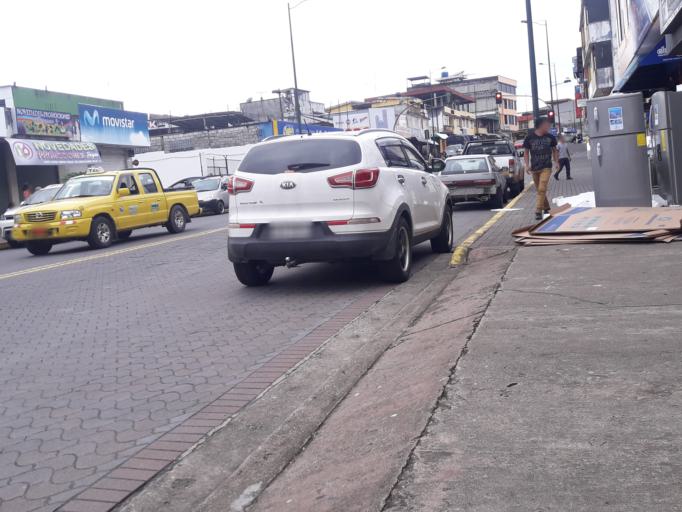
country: EC
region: Napo
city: Tena
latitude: -0.9969
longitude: -77.8127
